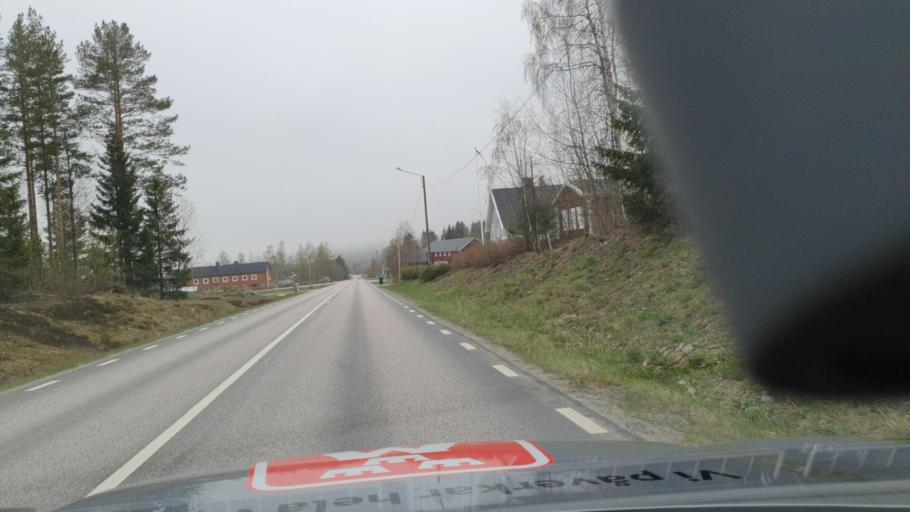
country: SE
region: Vaesternorrland
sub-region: OErnskoeldsviks Kommun
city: Ornskoldsvik
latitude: 63.3627
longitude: 18.8636
